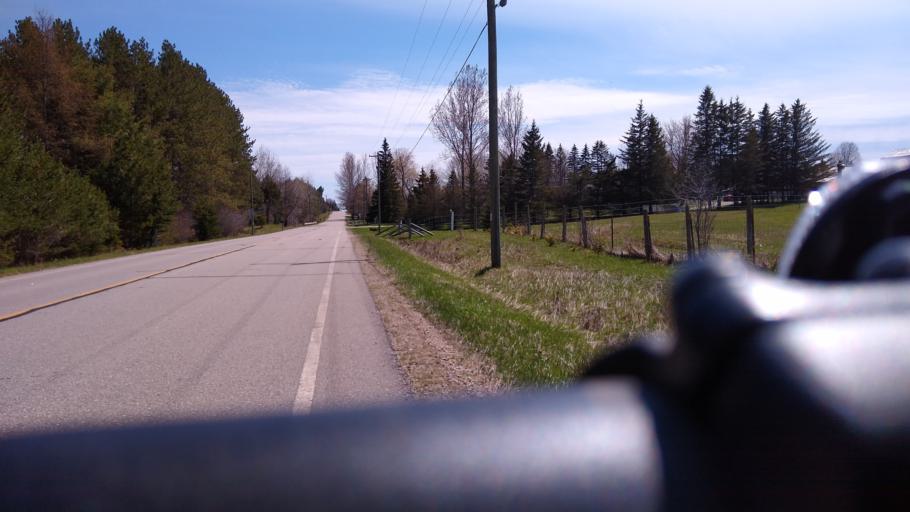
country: US
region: Michigan
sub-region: Delta County
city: Escanaba
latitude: 45.7263
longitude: -87.2025
